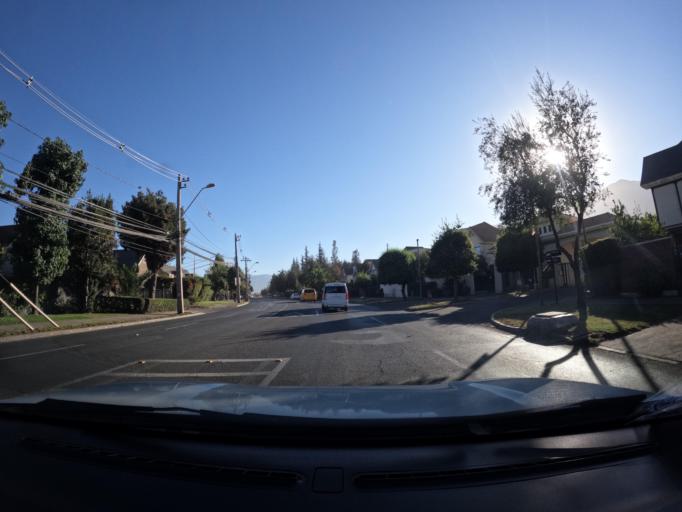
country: CL
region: Santiago Metropolitan
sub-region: Provincia de Santiago
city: Villa Presidente Frei, Nunoa, Santiago, Chile
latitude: -33.4828
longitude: -70.5461
